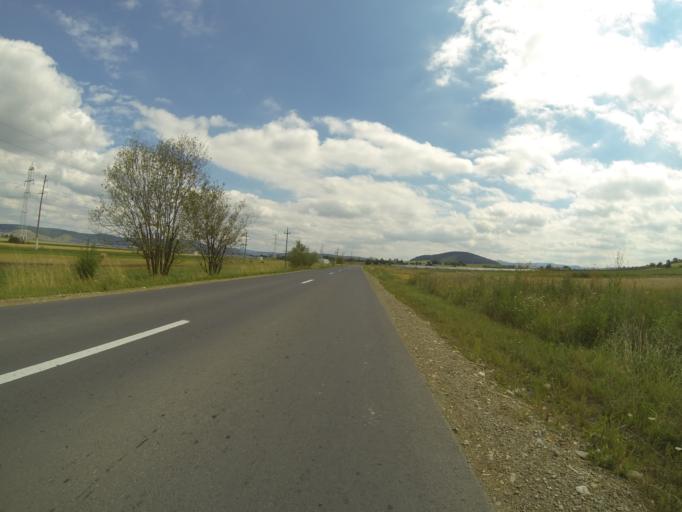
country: RO
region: Brasov
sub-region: Comuna Hoghiz
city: Hoghiz
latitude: 45.9756
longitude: 25.3079
